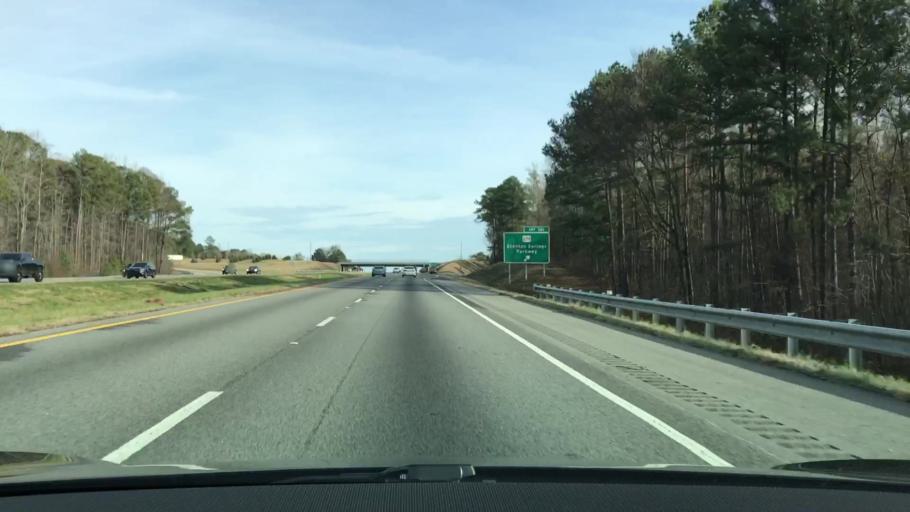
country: US
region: Georgia
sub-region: Walton County
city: Social Circle
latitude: 33.6104
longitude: -83.7059
